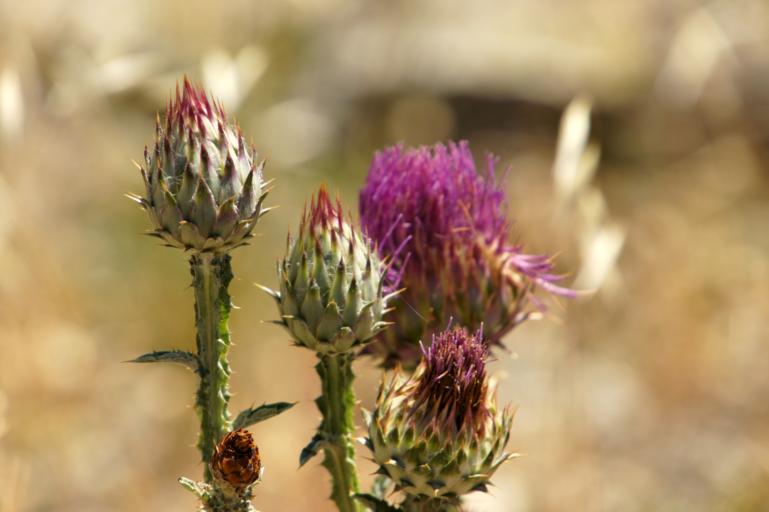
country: FR
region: Corsica
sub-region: Departement de la Haute-Corse
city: Corte
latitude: 42.3572
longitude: 9.0573
